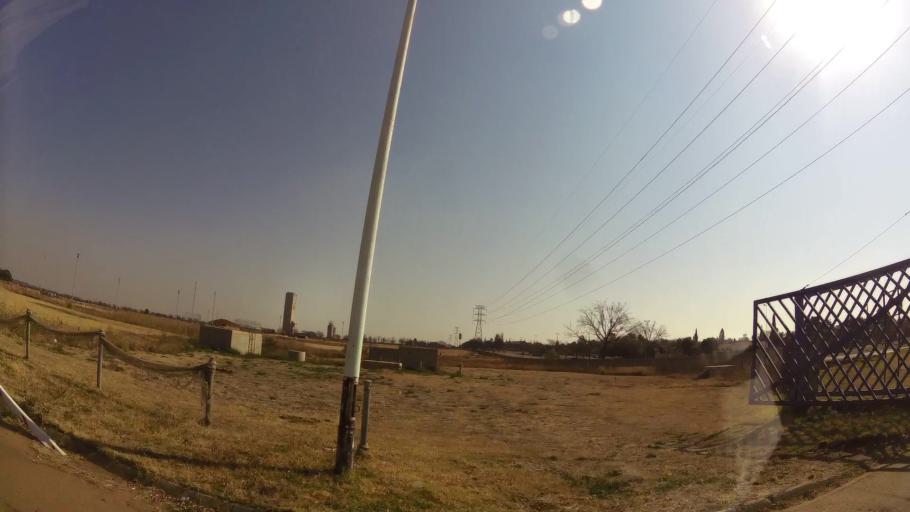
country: ZA
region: Gauteng
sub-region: Ekurhuleni Metropolitan Municipality
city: Boksburg
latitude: -26.2335
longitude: 28.2760
